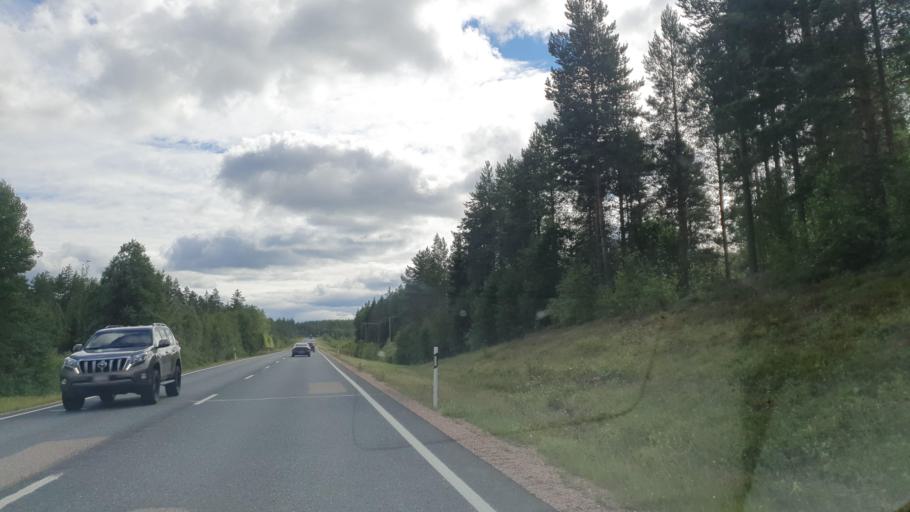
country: FI
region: Kainuu
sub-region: Kajaani
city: Kajaani
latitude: 64.1056
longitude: 27.4483
